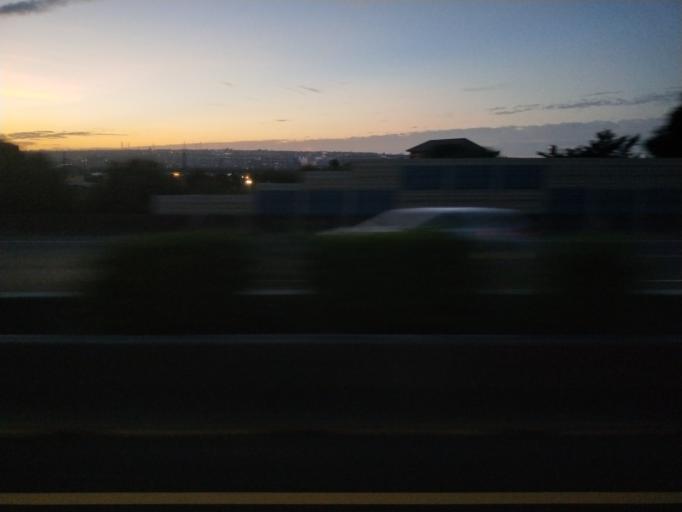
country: TW
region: Taiwan
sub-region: Taichung City
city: Taichung
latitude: 24.1914
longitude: 120.6392
